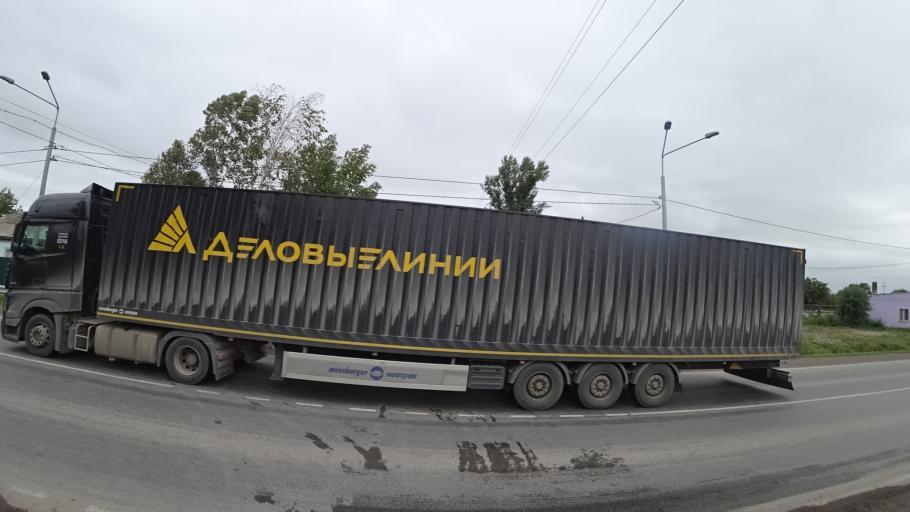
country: RU
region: Primorskiy
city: Chernigovka
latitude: 44.3406
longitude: 132.5883
